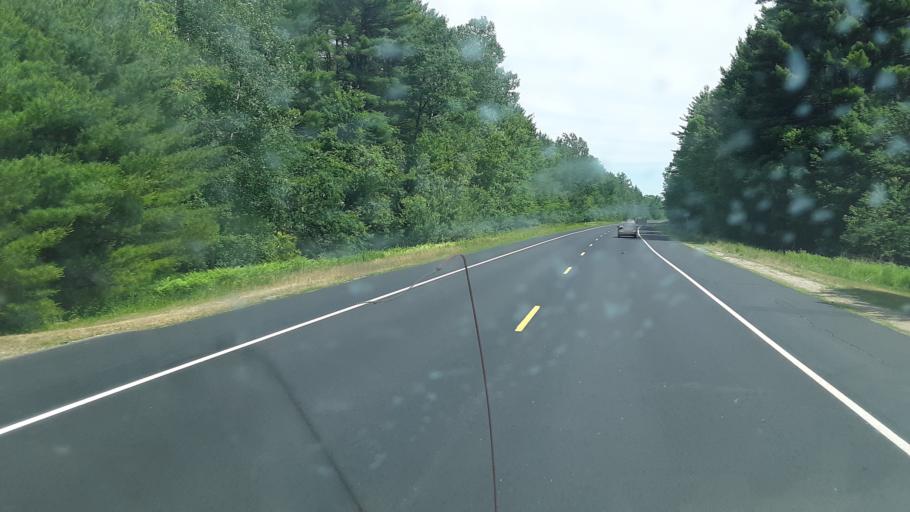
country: US
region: Maine
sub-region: Somerset County
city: Norridgewock
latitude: 44.6851
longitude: -69.7305
